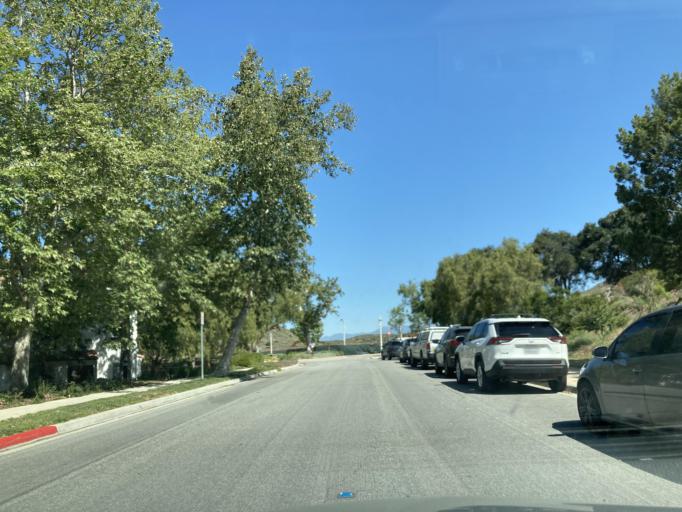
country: US
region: California
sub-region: Ventura County
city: Camarillo
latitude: 34.1684
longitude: -119.0344
